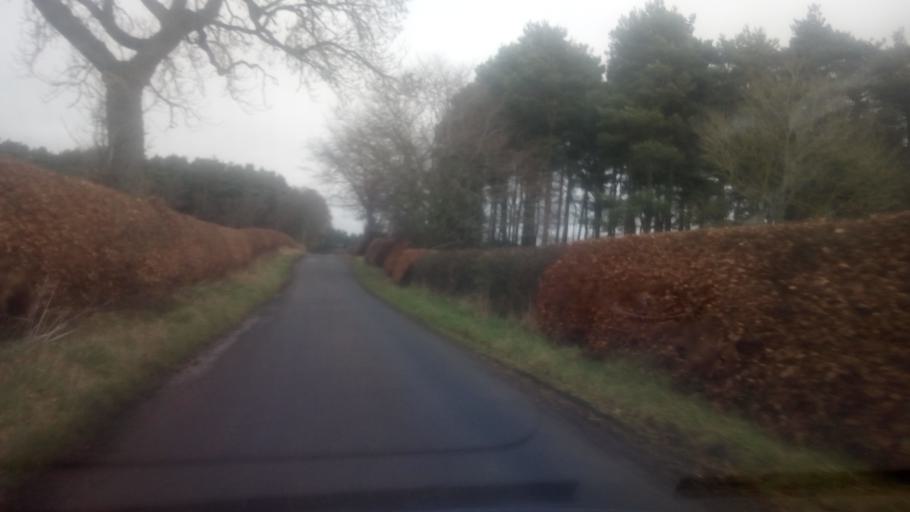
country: GB
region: Scotland
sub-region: The Scottish Borders
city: Kelso
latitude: 55.5423
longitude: -2.4932
